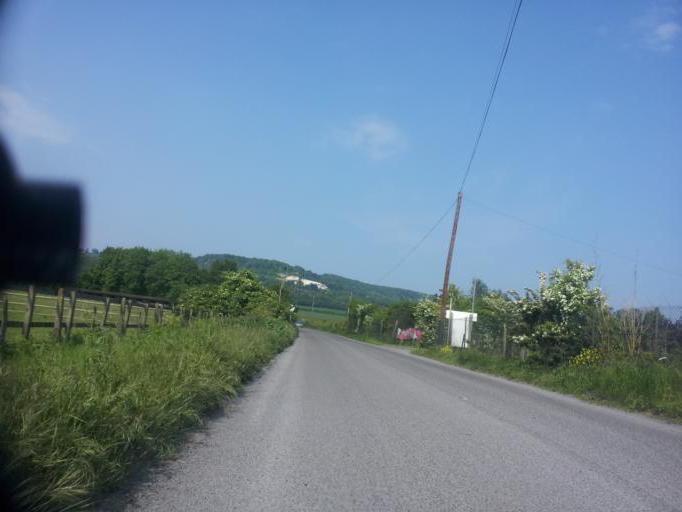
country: GB
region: England
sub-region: Kent
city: Aylesford
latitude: 51.3106
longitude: 0.4928
